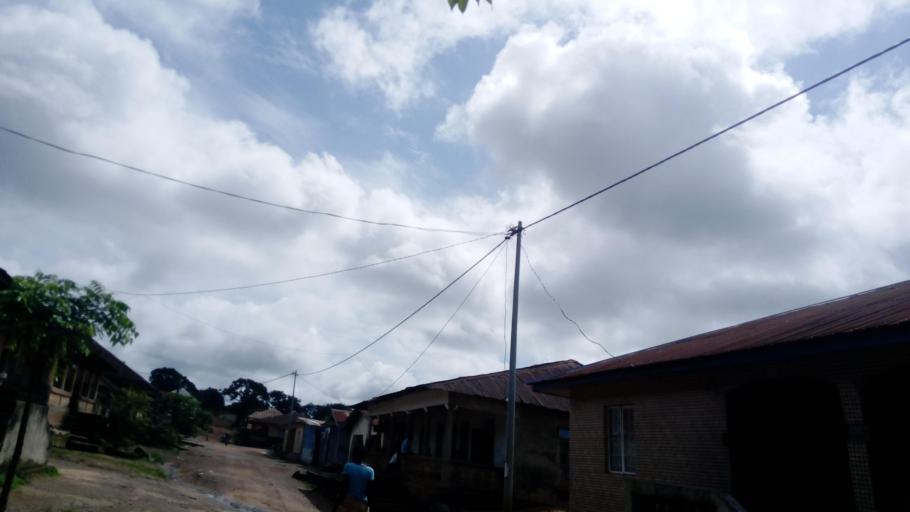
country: SL
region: Northern Province
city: Makeni
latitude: 8.8889
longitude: -12.0387
